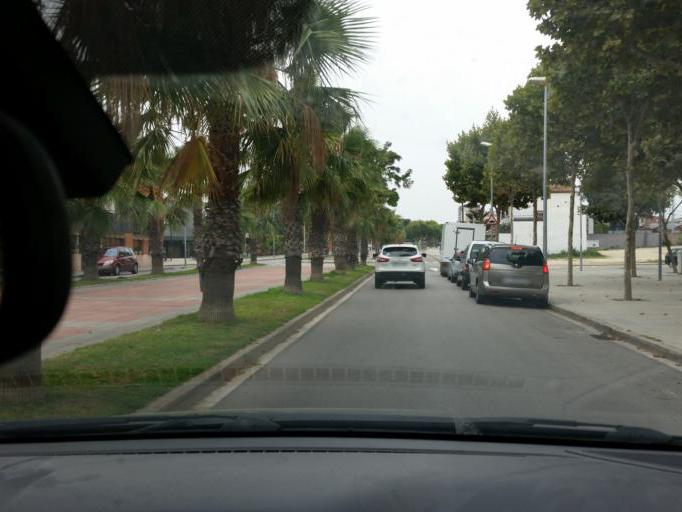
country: ES
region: Catalonia
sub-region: Provincia de Barcelona
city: Vilassar de Mar
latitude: 41.5106
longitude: 2.3962
